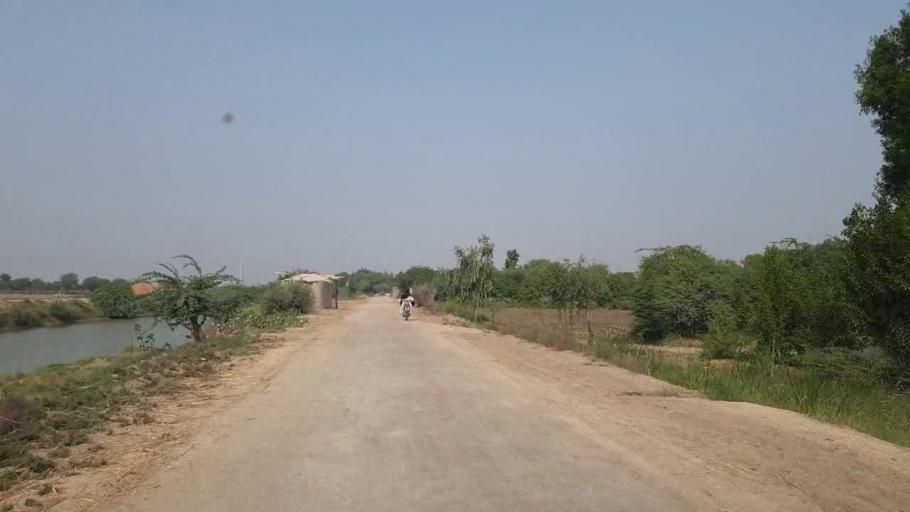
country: PK
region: Sindh
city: Kario
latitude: 24.9219
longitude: 68.6010
